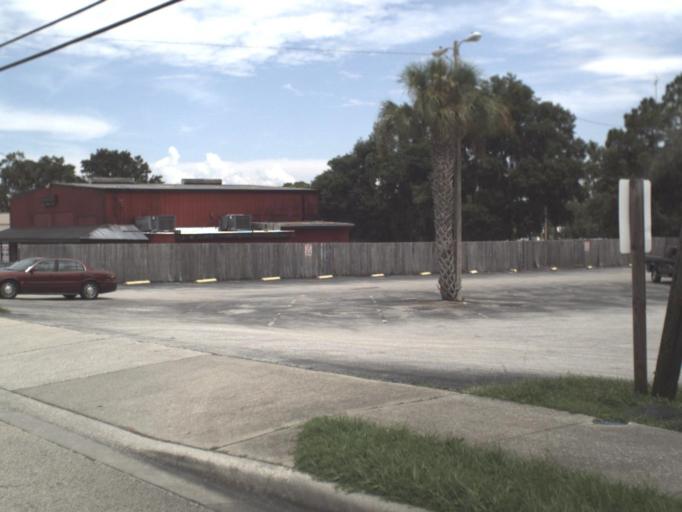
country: US
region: Florida
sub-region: Citrus County
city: Inverness
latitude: 28.8359
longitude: -82.3412
